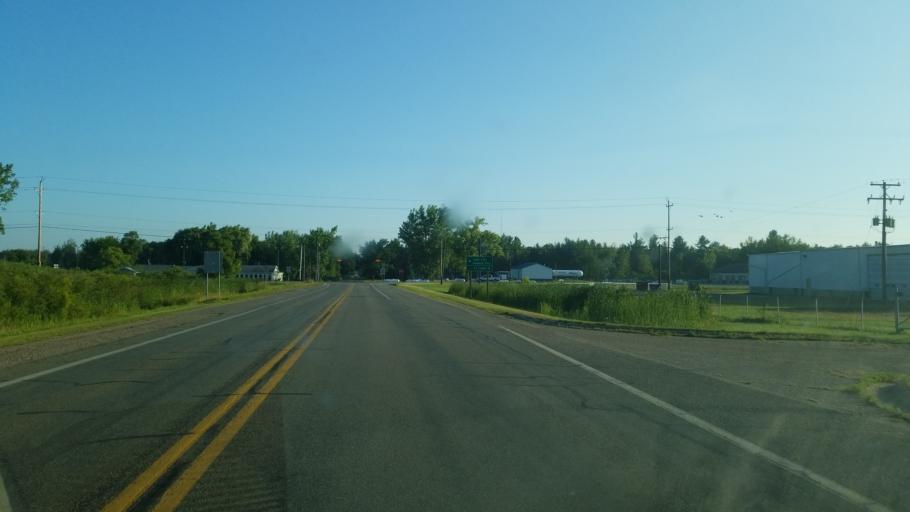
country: US
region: Michigan
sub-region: Montcalm County
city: Edmore
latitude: 43.4065
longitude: -85.0847
